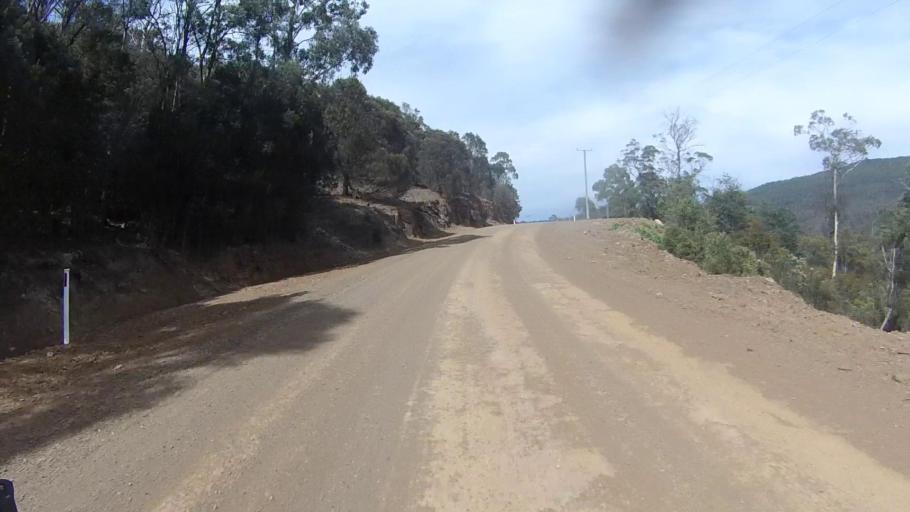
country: AU
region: Tasmania
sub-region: Sorell
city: Sorell
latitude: -42.6679
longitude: 147.8866
